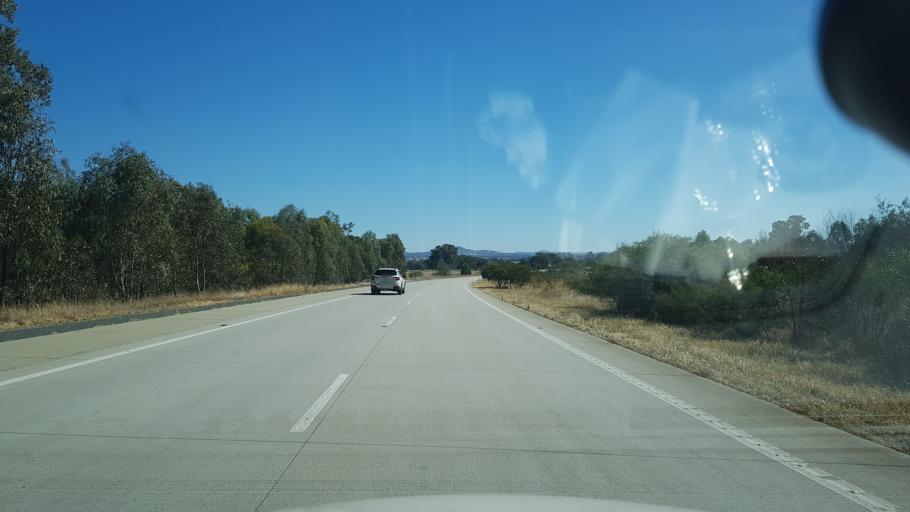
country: AU
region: New South Wales
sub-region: Albury Municipality
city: Lavington
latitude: -35.9264
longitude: 147.0865
